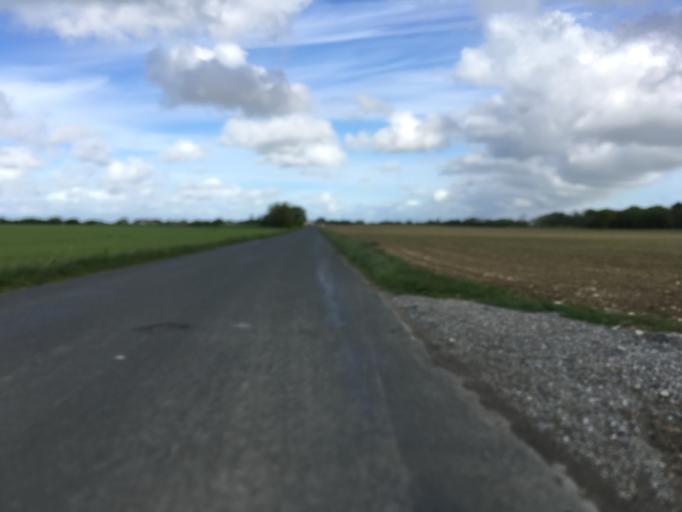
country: FR
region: Poitou-Charentes
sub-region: Departement de la Charente-Maritime
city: Verines
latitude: 46.1768
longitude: -0.9672
